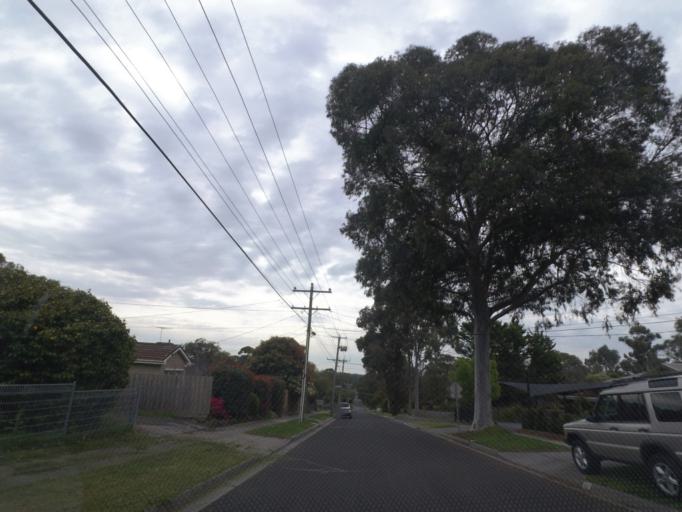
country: AU
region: Victoria
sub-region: Knox
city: The Basin
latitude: -37.8602
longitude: 145.3032
